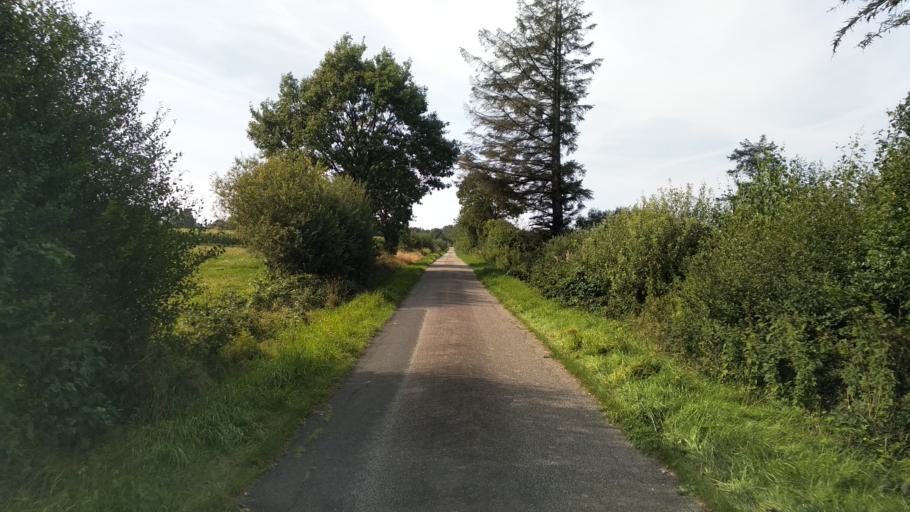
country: DE
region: Schleswig-Holstein
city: Bredstedt
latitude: 54.6466
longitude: 8.9632
